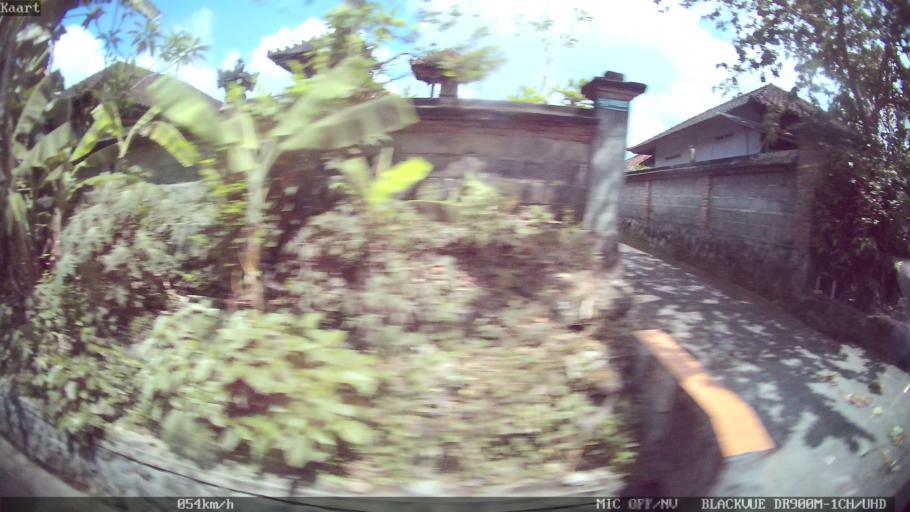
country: ID
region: Bali
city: Banjar Pasekan
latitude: -8.5897
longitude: 115.2966
